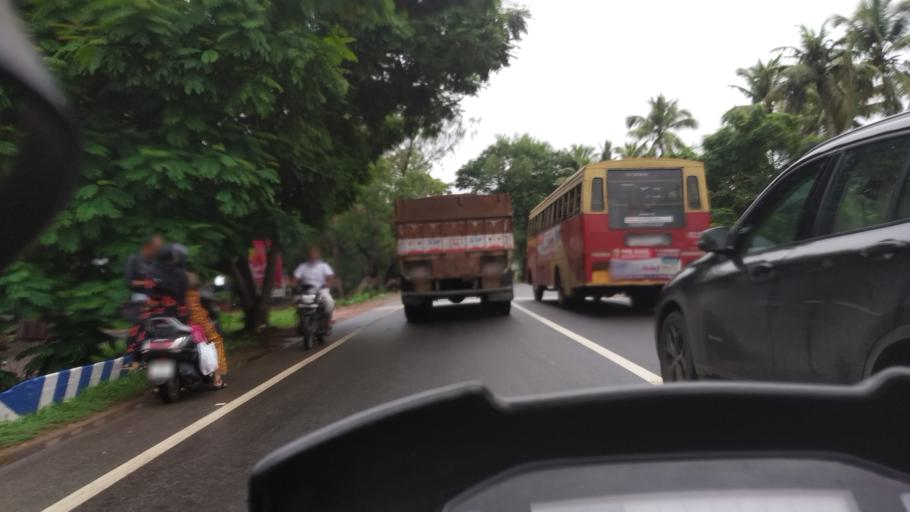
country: IN
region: Kerala
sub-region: Alappuzha
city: Mavelikara
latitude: 9.2944
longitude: 76.4343
